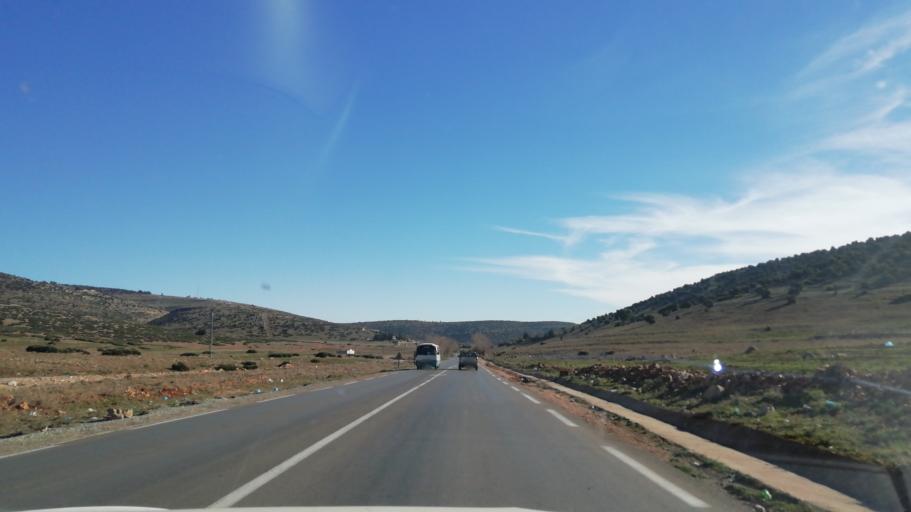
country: DZ
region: Tlemcen
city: Sebdou
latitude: 34.7138
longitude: -1.3257
